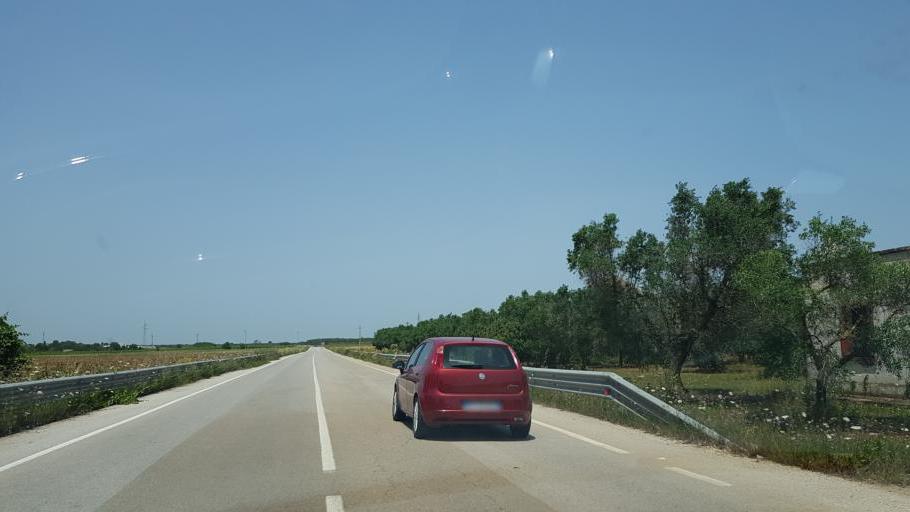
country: IT
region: Apulia
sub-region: Provincia di Brindisi
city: San Pancrazio Salentino
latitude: 40.4763
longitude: 17.8370
